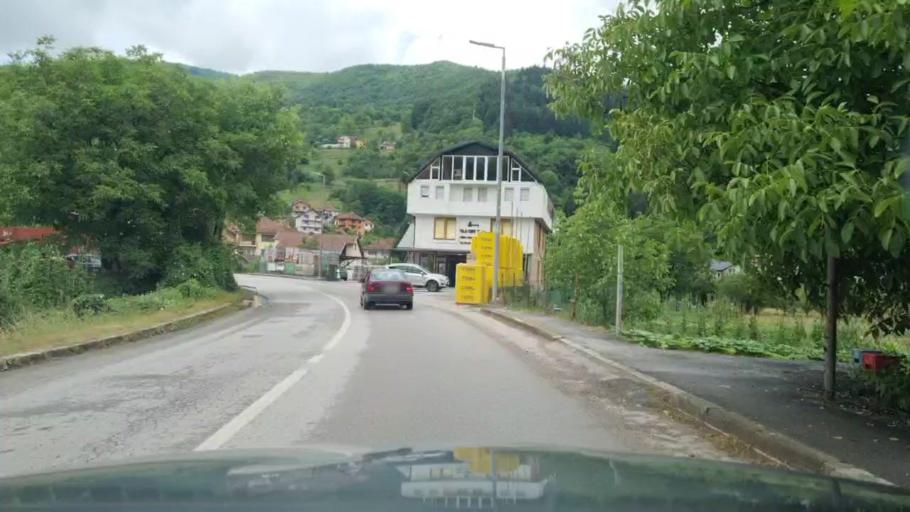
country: BA
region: Federation of Bosnia and Herzegovina
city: Gorazde
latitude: 43.6539
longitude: 18.9653
